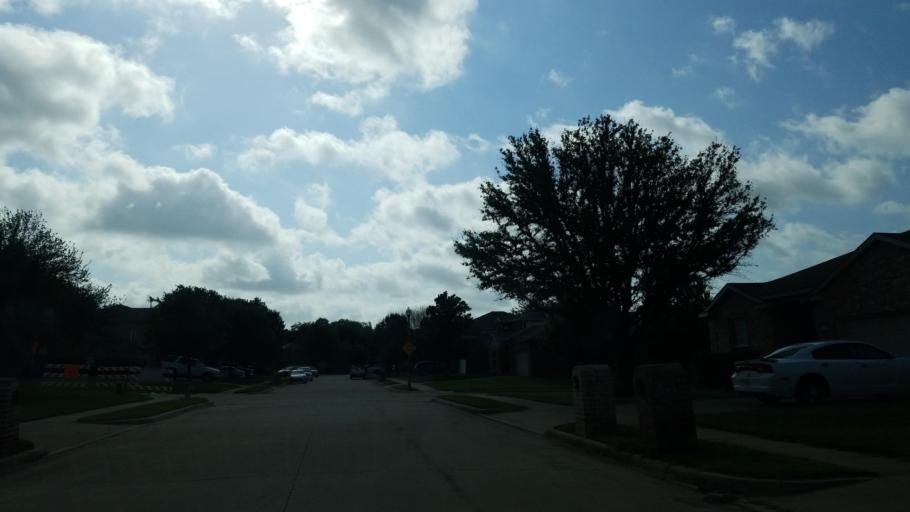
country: US
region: Texas
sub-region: Denton County
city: Corinth
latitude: 33.1464
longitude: -97.1154
